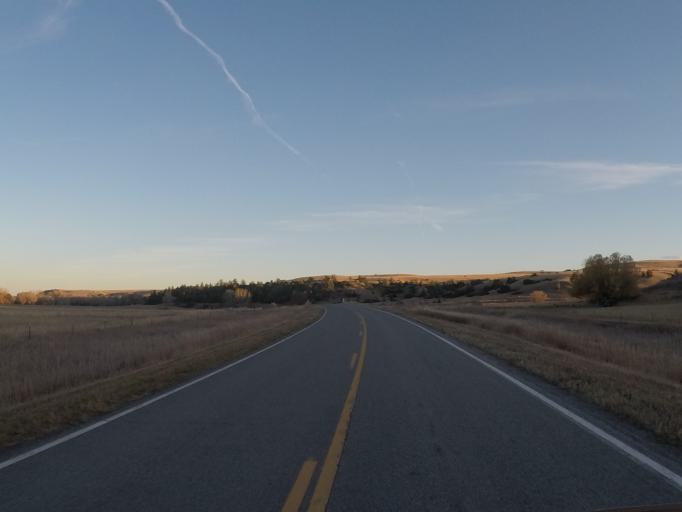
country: US
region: Montana
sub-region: Sweet Grass County
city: Big Timber
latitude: 45.7882
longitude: -109.8513
